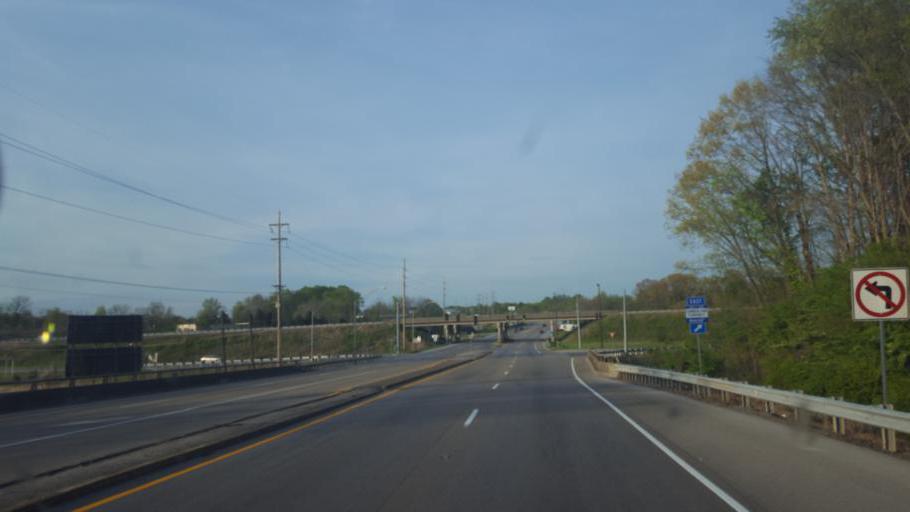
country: US
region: Kentucky
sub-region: Barren County
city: Glasgow
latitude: 36.9765
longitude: -85.9363
